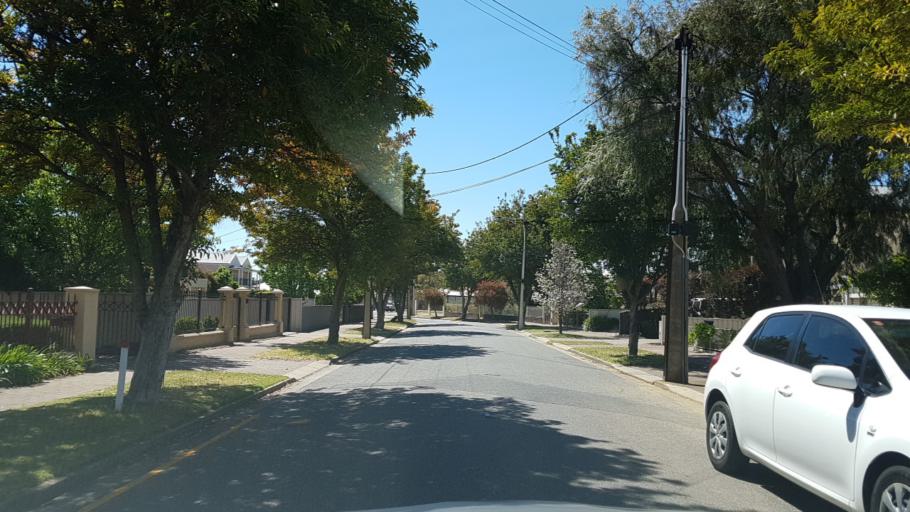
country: AU
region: South Australia
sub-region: Holdfast Bay
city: Glenelg East
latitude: -34.9744
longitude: 138.5211
